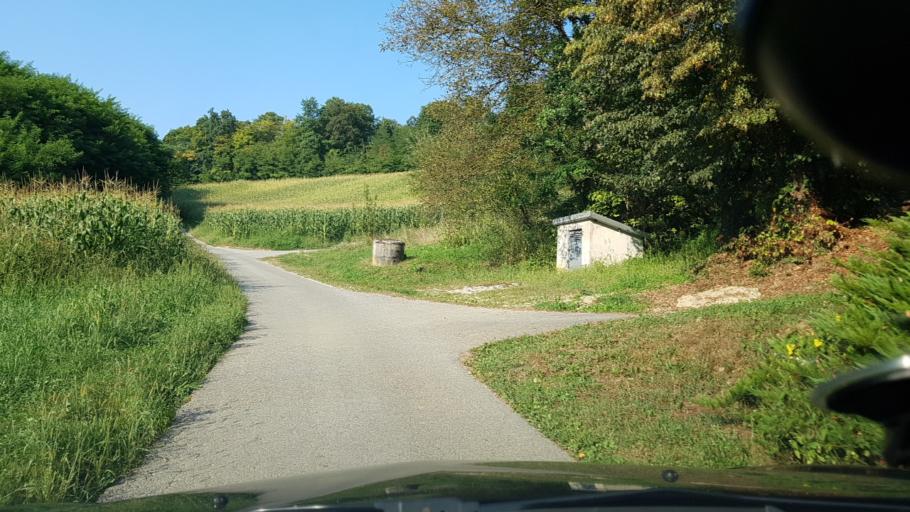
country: HR
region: Krapinsko-Zagorska
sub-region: Grad Krapina
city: Krapina
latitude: 46.1330
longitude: 15.8504
